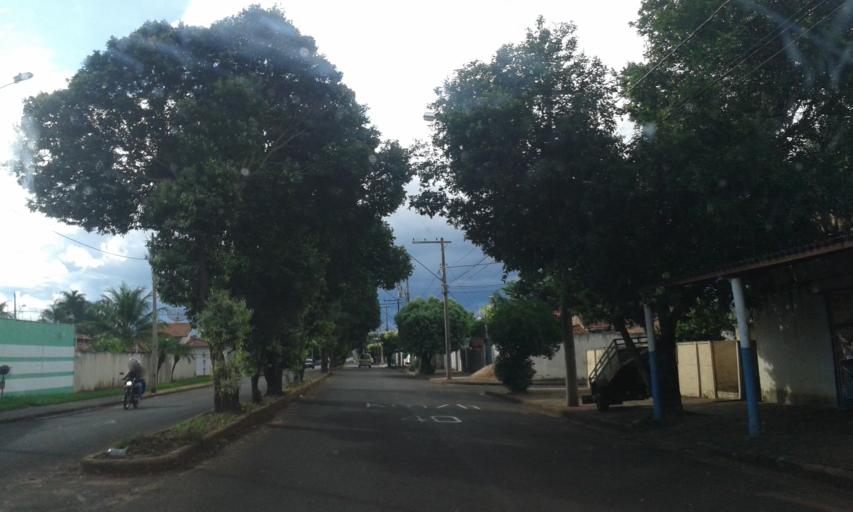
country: BR
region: Minas Gerais
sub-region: Ituiutaba
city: Ituiutaba
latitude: -18.9674
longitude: -49.4482
